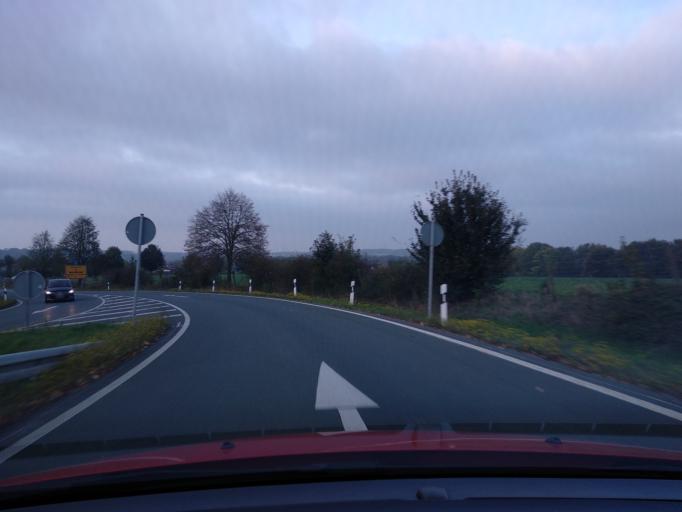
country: DE
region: North Rhine-Westphalia
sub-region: Regierungsbezirk Detmold
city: Paderborn
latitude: 51.6484
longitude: 8.7192
